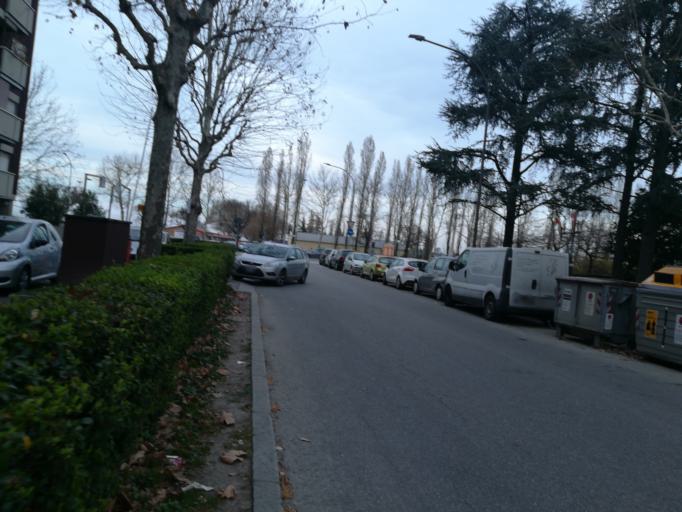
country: IT
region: Emilia-Romagna
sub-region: Provincia di Bologna
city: Progresso
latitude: 44.5492
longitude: 11.3620
